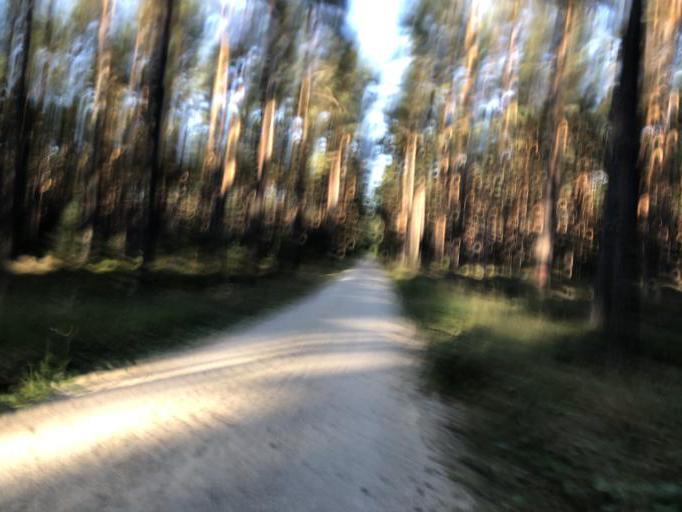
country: DE
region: Bavaria
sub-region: Regierungsbezirk Mittelfranken
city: Uttenreuth
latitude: 49.5704
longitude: 11.0805
